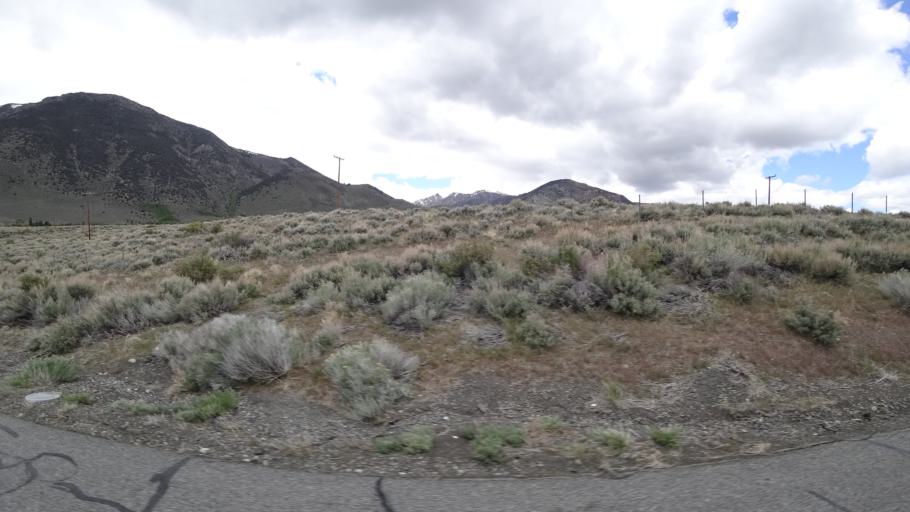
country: US
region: California
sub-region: Mono County
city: Bridgeport
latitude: 38.0256
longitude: -119.1559
